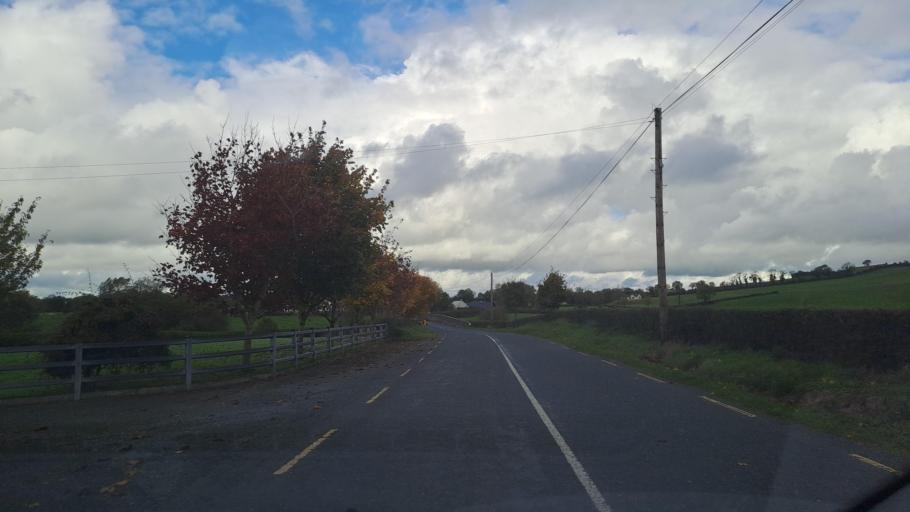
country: IE
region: Ulster
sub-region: An Cabhan
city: Mullagh
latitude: 53.8431
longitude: -6.9587
